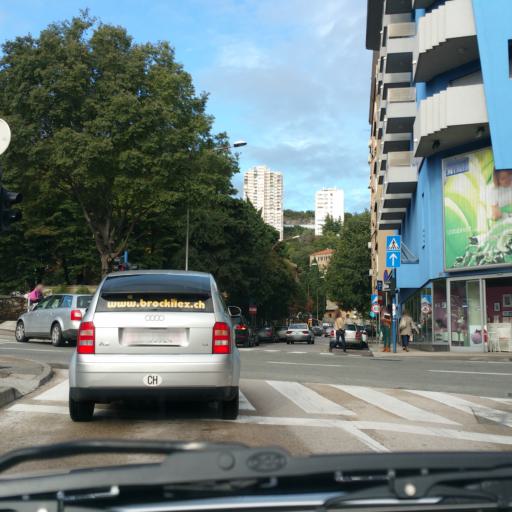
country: HR
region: Primorsko-Goranska
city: Drenova
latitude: 45.3327
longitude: 14.4308
